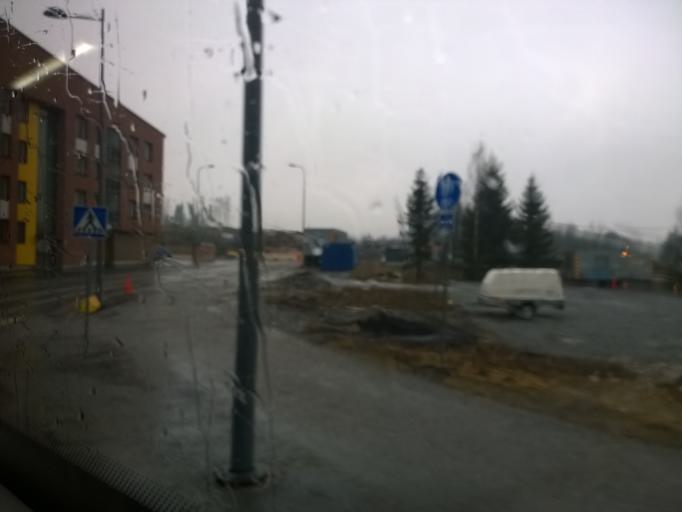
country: FI
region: Pirkanmaa
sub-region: Tampere
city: Tampere
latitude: 61.4348
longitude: 23.8080
